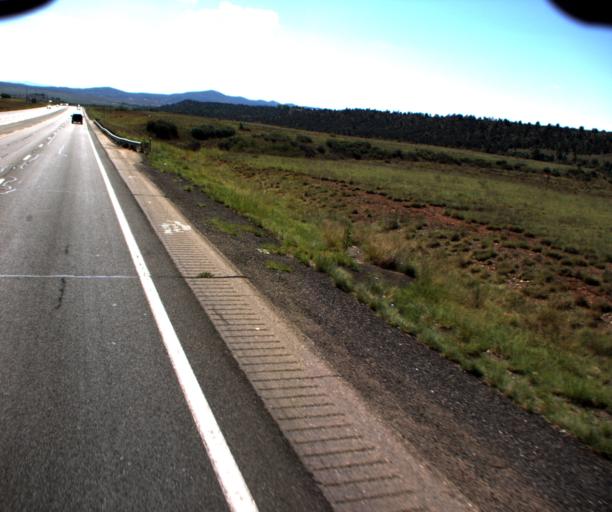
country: US
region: Arizona
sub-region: Yavapai County
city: Prescott Valley
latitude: 34.5784
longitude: -112.2948
